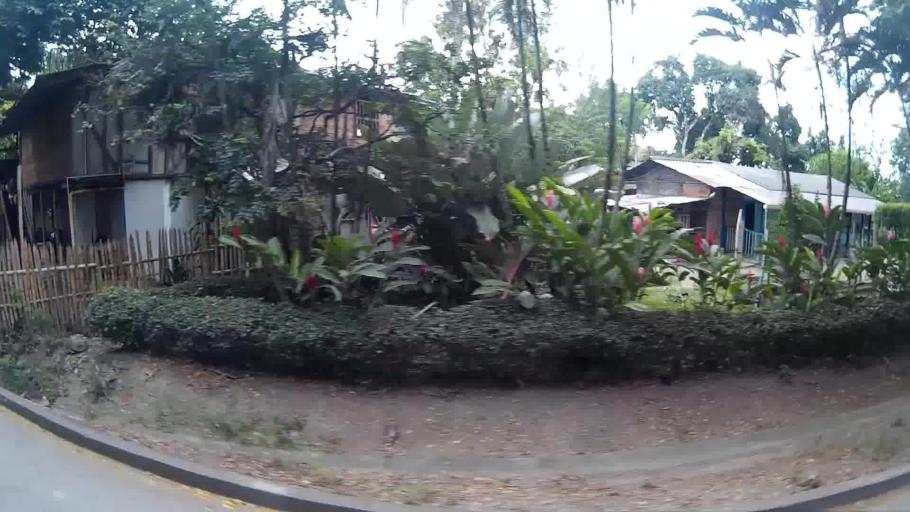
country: CO
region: Risaralda
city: La Virginia
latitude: 4.8994
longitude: -75.8788
